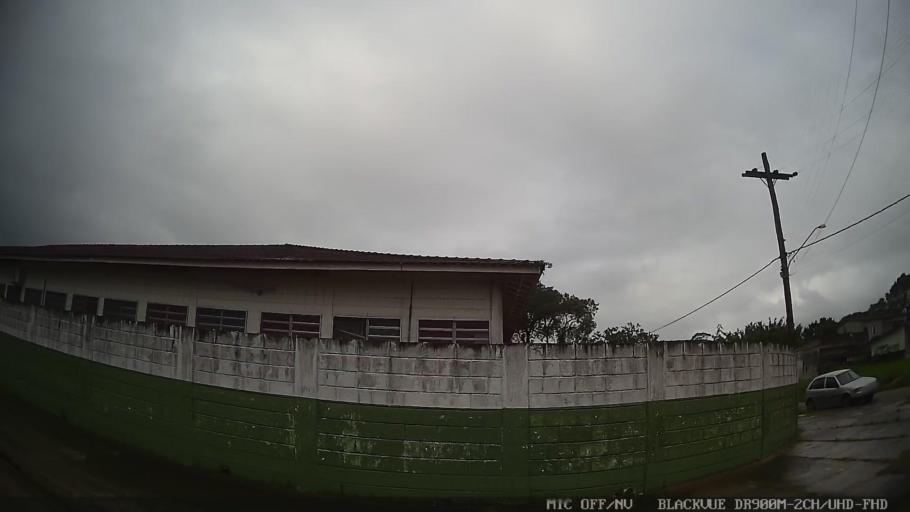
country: BR
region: Sao Paulo
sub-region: Itanhaem
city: Itanhaem
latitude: -24.1790
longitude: -46.8173
